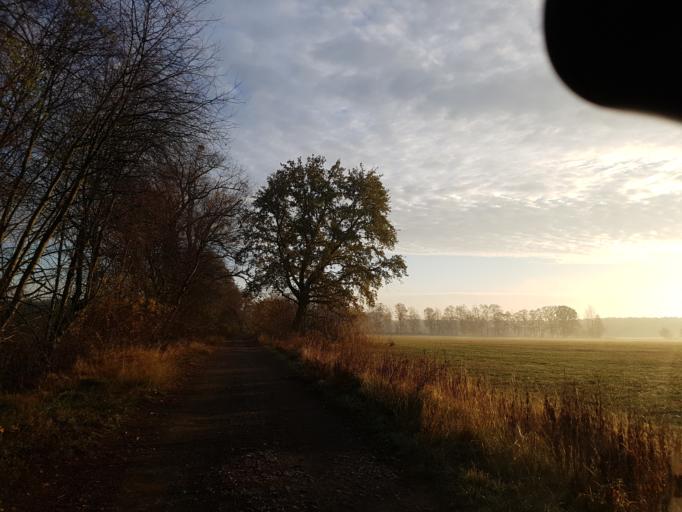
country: DE
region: Saxony-Anhalt
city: Elster
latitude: 51.8837
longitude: 12.8477
